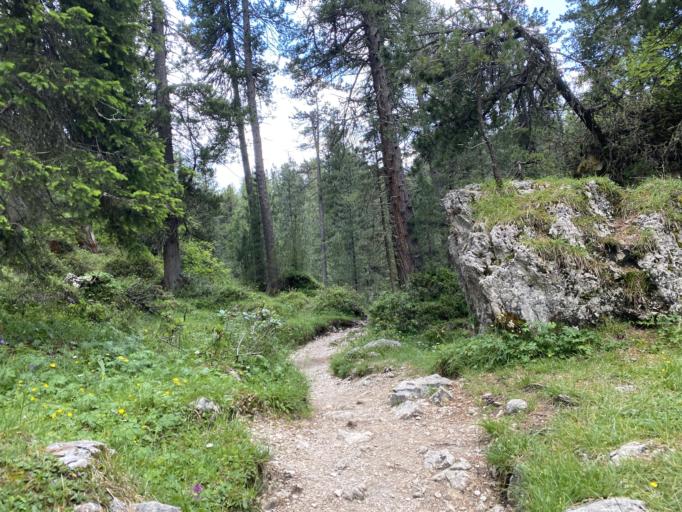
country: IT
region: Trentino-Alto Adige
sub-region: Bolzano
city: Selva
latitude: 46.6226
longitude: 11.7713
